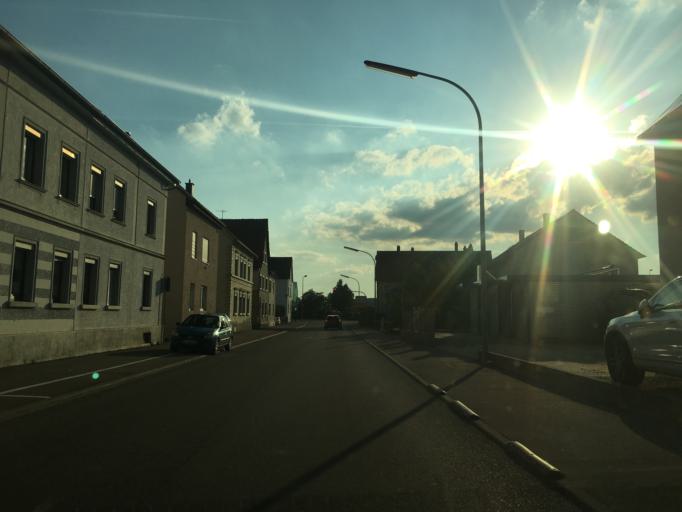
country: DE
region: Baden-Wuerttemberg
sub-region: Tuebingen Region
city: Ehingen
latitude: 48.2859
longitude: 9.7211
